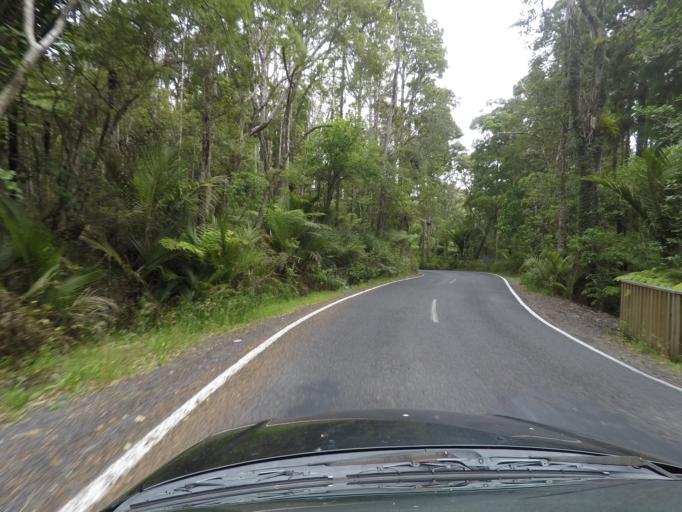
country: NZ
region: Auckland
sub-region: Auckland
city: Titirangi
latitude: -36.9488
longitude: 174.6585
